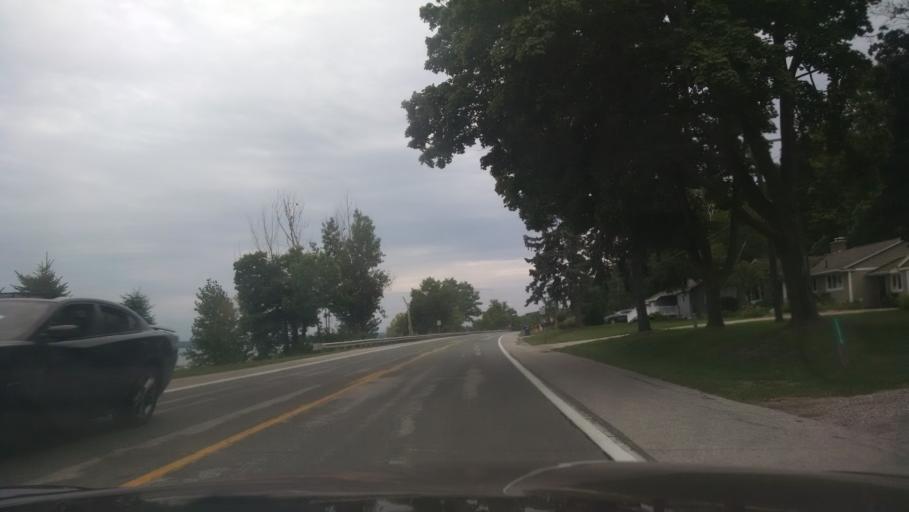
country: US
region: Michigan
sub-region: Leelanau County
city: Greilickville
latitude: 44.8164
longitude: -85.6443
